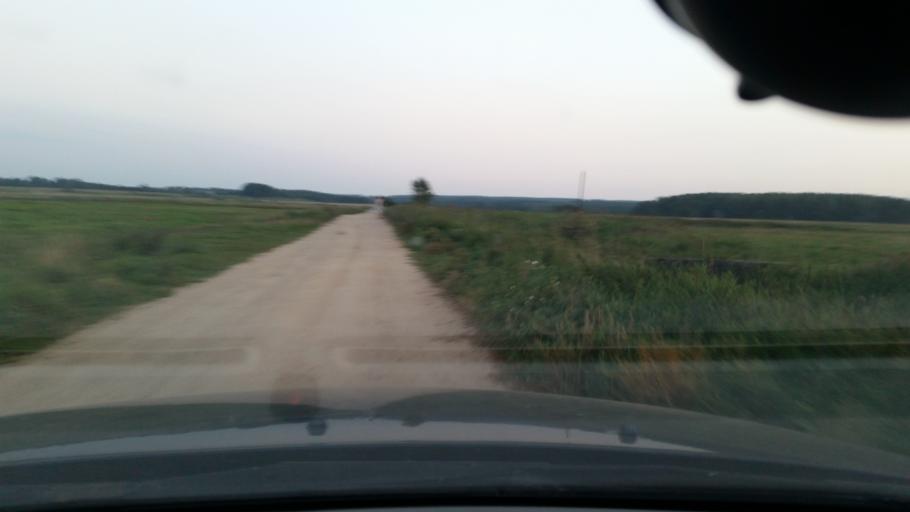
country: PL
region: Pomeranian Voivodeship
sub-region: Powiat wejherowski
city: Choczewo
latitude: 54.7860
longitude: 17.7946
